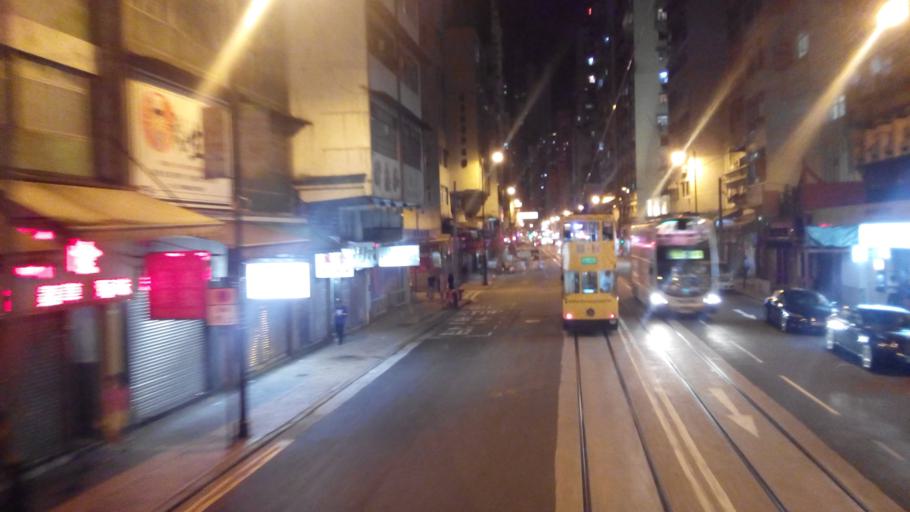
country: HK
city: Hong Kong
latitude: 22.2878
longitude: 114.1459
